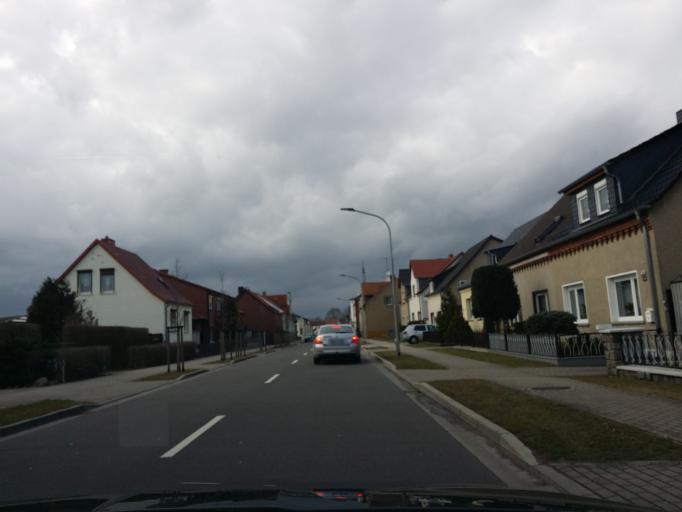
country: DE
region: Saxony-Anhalt
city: Goldbeck
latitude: 52.7151
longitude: 11.8648
